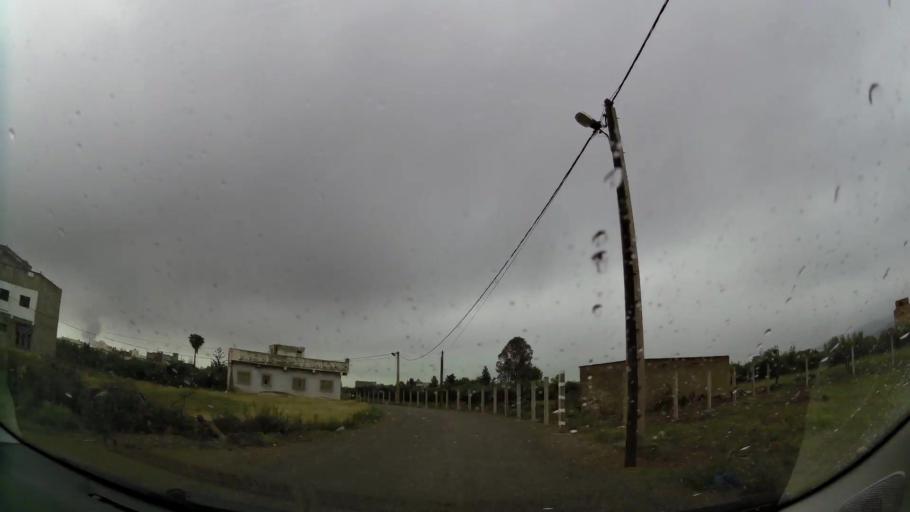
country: MA
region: Oriental
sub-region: Nador
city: Nador
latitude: 35.1545
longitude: -2.9587
